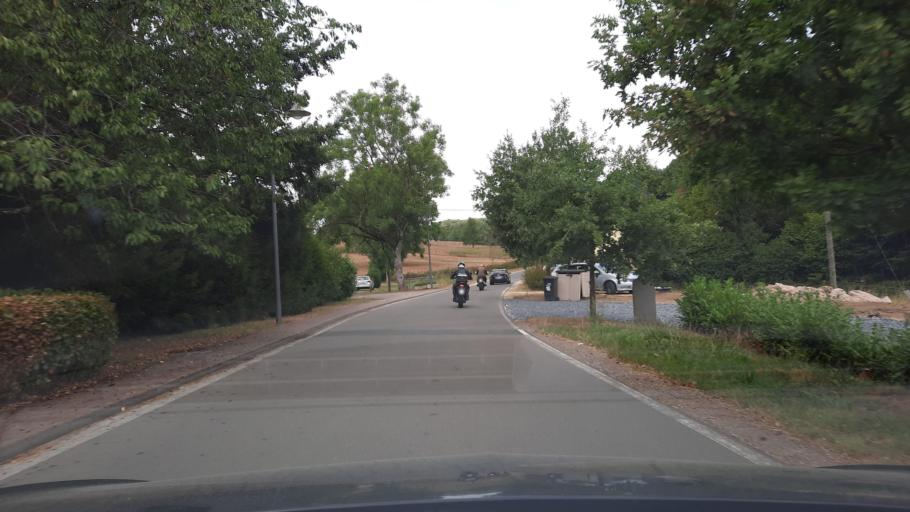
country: DE
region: Rheinland-Pfalz
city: Watzerath
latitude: 50.1935
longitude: 6.3674
